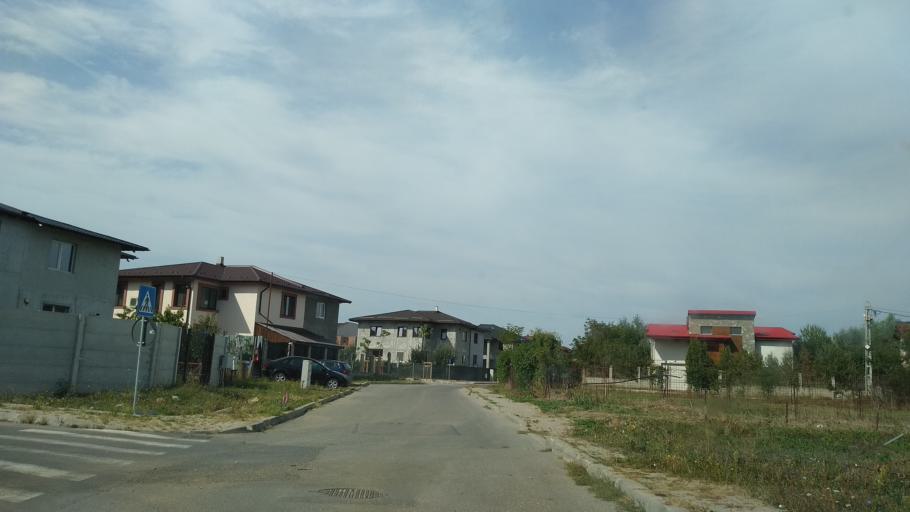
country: RO
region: Ilfov
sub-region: Comuna Chitila
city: Chitila
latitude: 44.5144
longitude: 25.9876
